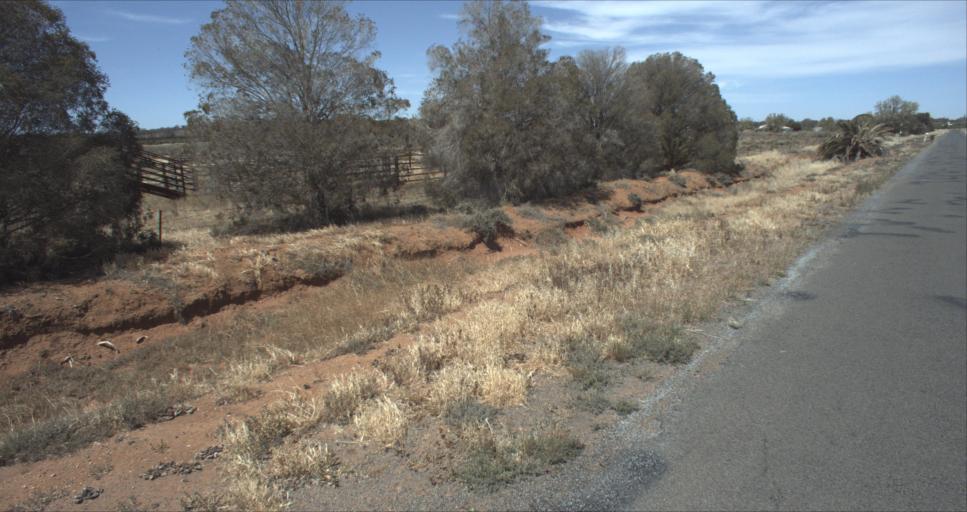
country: AU
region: New South Wales
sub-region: Leeton
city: Leeton
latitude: -34.6023
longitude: 146.4267
